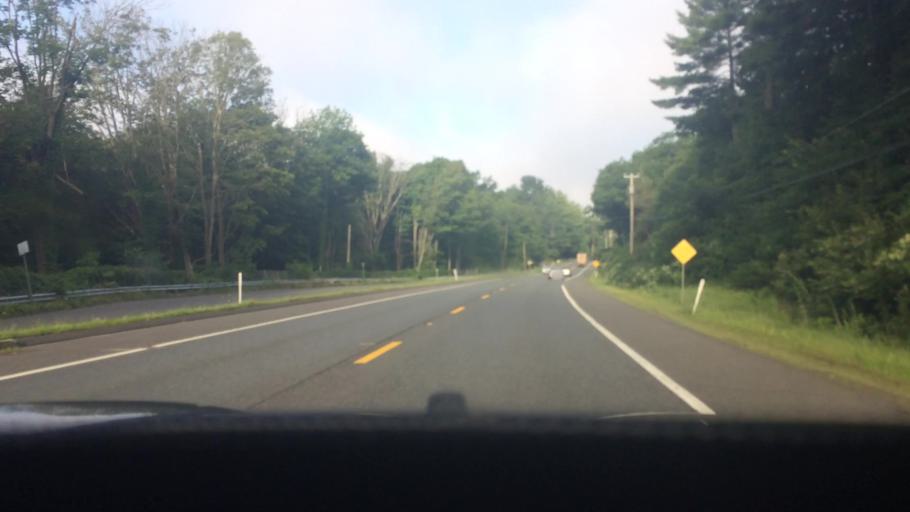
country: US
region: Massachusetts
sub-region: Franklin County
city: Turners Falls
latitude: 42.6064
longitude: -72.5223
